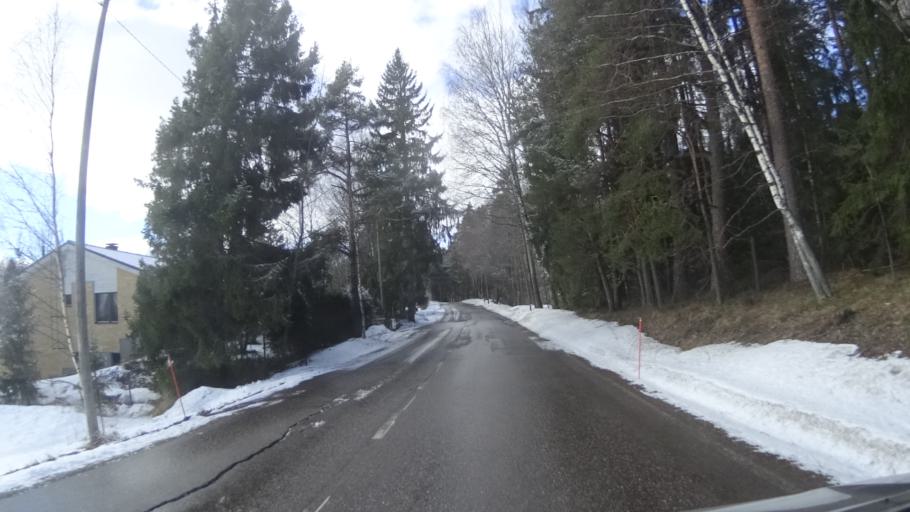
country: FI
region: Uusimaa
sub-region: Helsinki
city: Vantaa
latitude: 60.2526
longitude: 25.1688
